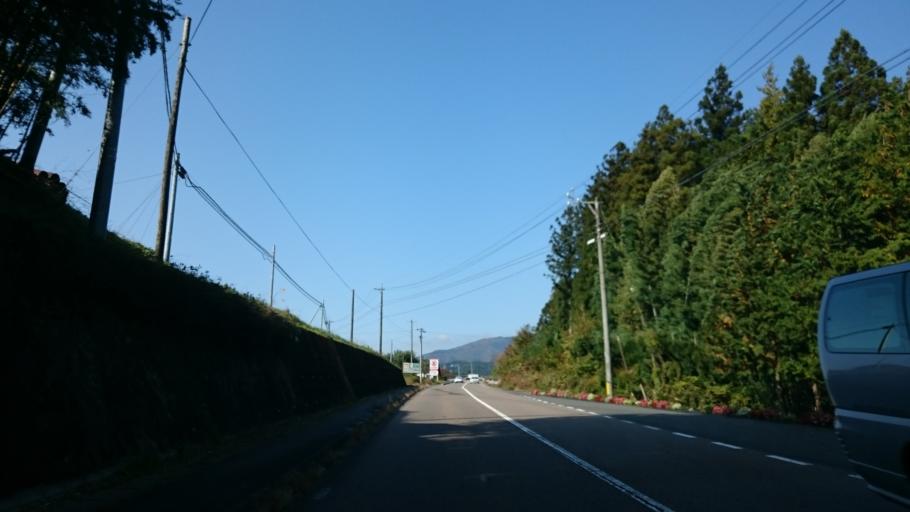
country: JP
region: Gifu
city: Nakatsugawa
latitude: 35.7385
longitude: 137.3424
